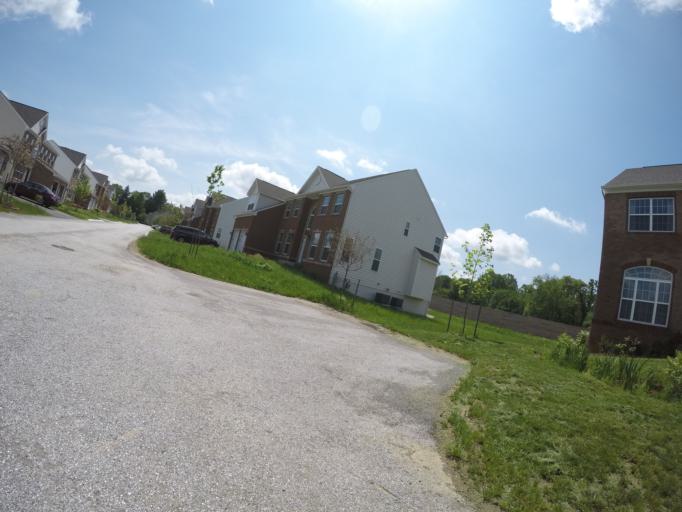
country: US
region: Maryland
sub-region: Howard County
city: Ellicott City
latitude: 39.2972
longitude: -76.8423
